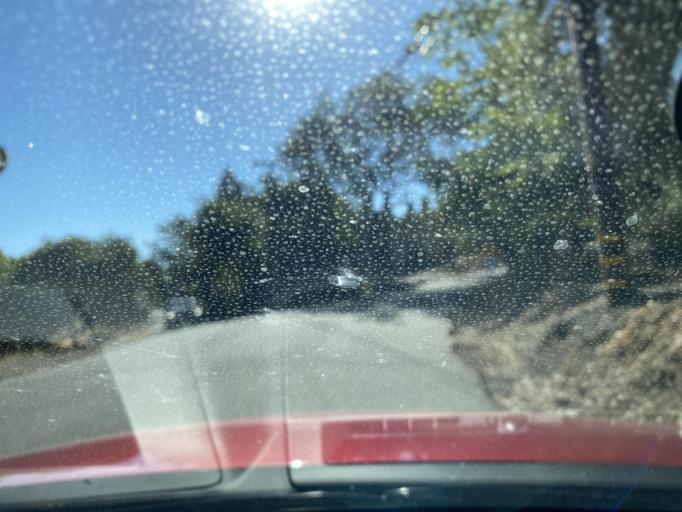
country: US
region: California
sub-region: Placer County
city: Auburn
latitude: 38.8935
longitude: -121.0679
